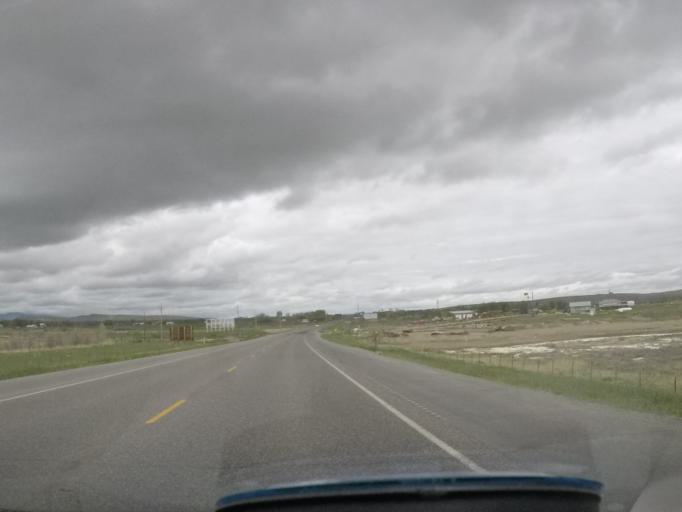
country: US
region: Wyoming
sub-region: Fremont County
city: Lander
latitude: 42.8666
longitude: -108.7780
